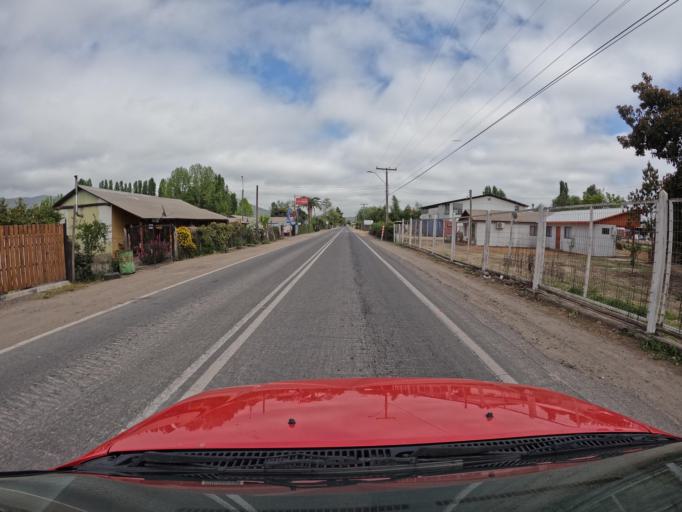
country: CL
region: O'Higgins
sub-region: Provincia de Colchagua
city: Santa Cruz
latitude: -34.6891
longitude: -71.3210
